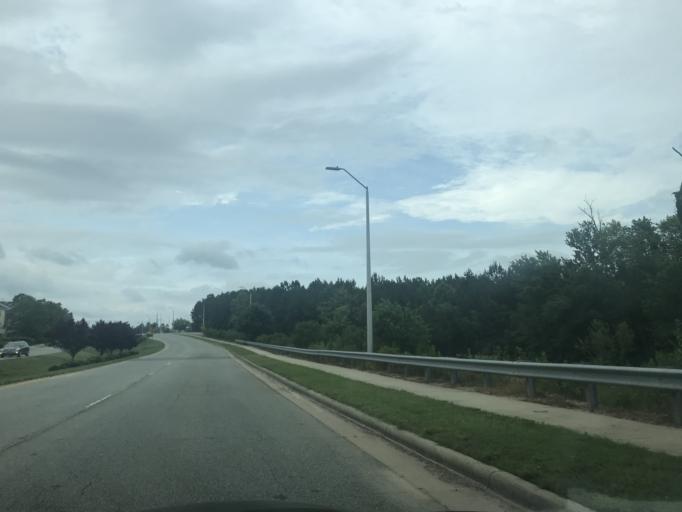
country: US
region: North Carolina
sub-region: Wake County
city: Green Level
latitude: 35.8161
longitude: -78.9026
